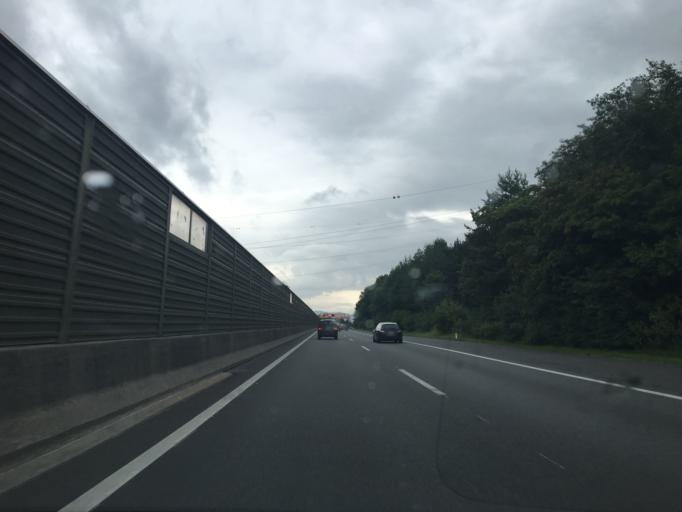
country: AT
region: Tyrol
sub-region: Politischer Bezirk Innsbruck Land
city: Hall in Tirol
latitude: 47.2729
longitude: 11.5008
